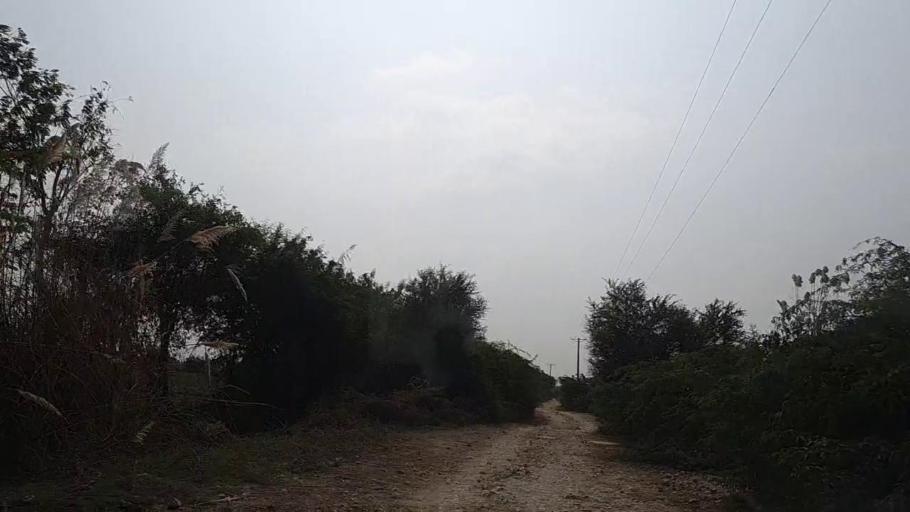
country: PK
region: Sindh
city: Mirpur Sakro
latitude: 24.6267
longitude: 67.7455
